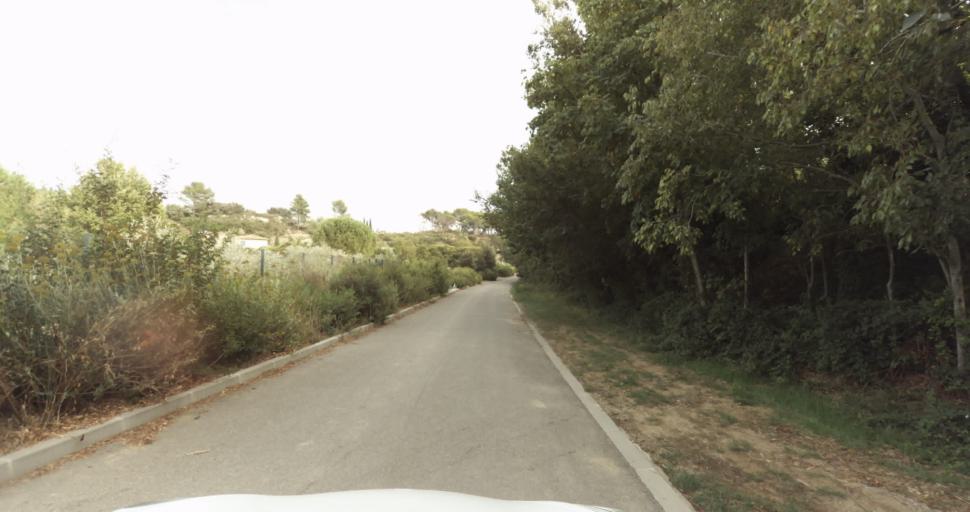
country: FR
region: Provence-Alpes-Cote d'Azur
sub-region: Departement des Bouches-du-Rhone
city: Miramas
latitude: 43.5769
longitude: 5.0205
